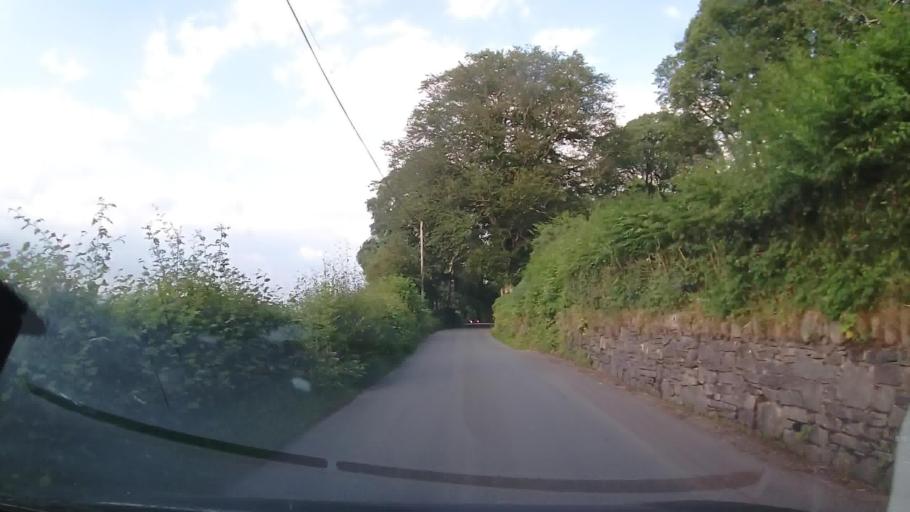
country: GB
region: Wales
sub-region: Gwynedd
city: Bala
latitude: 52.8900
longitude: -3.6104
